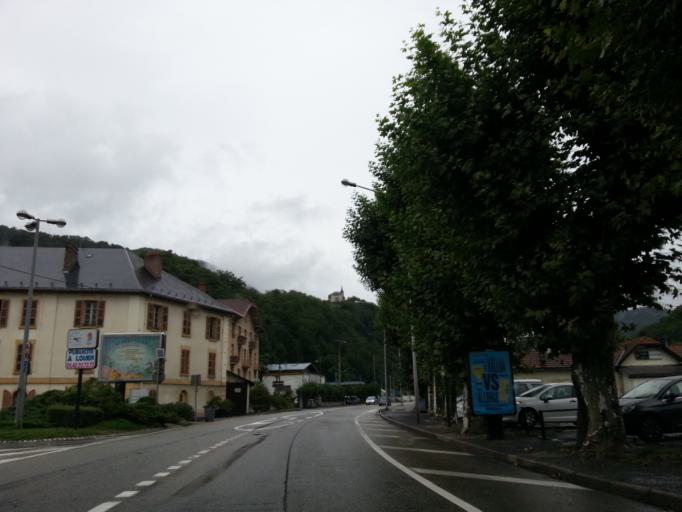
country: FR
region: Rhone-Alpes
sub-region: Departement de la Savoie
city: Albertville
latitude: 45.6791
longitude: 6.3940
